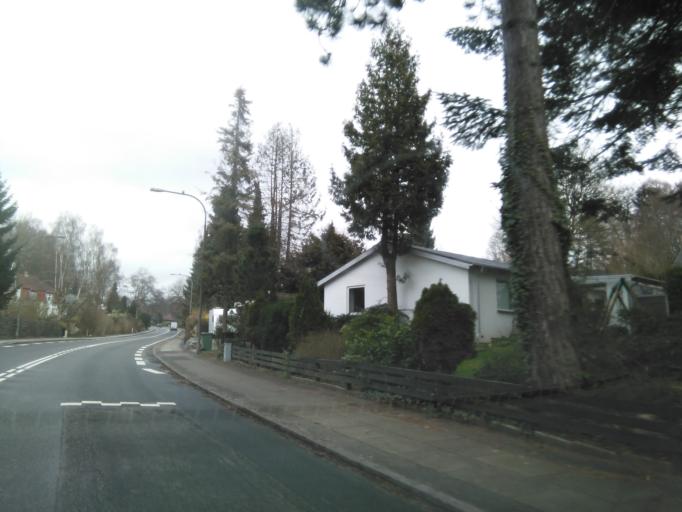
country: DK
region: Central Jutland
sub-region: Arhus Kommune
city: Stavtrup
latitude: 56.1586
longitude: 10.1005
